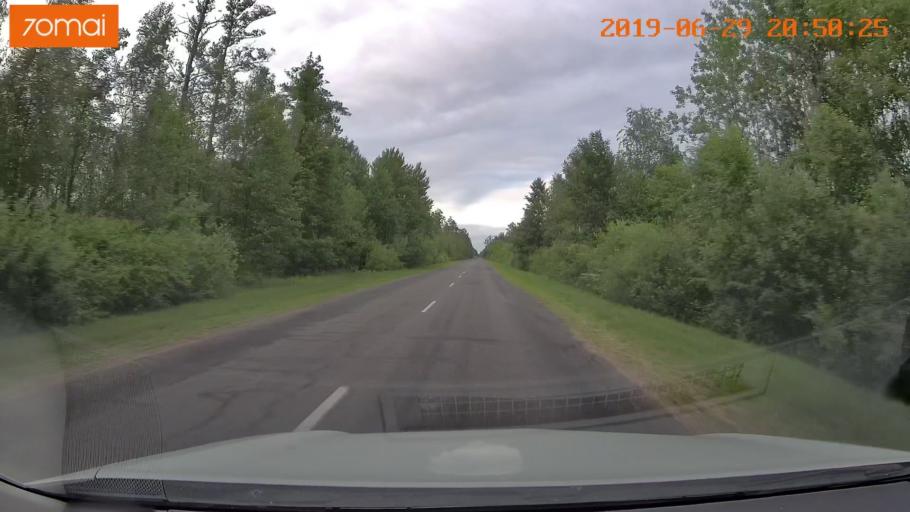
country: BY
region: Brest
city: Hantsavichy
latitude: 52.6762
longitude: 26.3355
